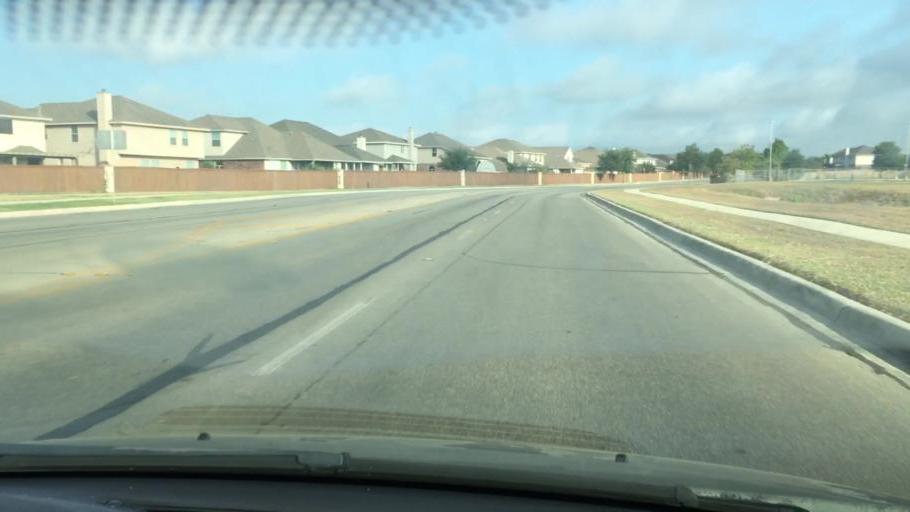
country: US
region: Texas
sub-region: Guadalupe County
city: Cibolo
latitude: 29.5717
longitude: -98.2385
